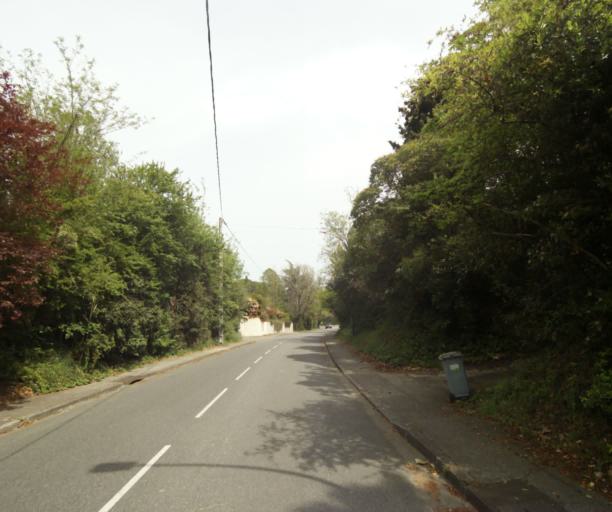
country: FR
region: Midi-Pyrenees
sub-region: Departement de la Haute-Garonne
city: Auzeville-Tolosane
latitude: 43.5265
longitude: 1.4880
